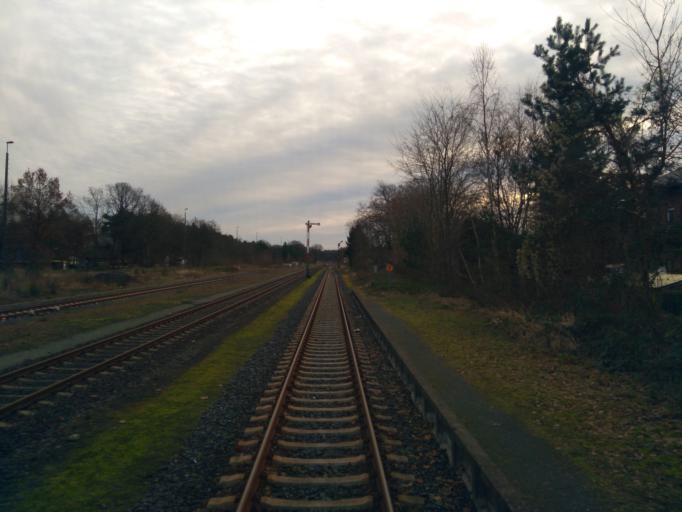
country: DE
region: Lower Saxony
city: Munster
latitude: 52.9931
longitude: 10.0973
